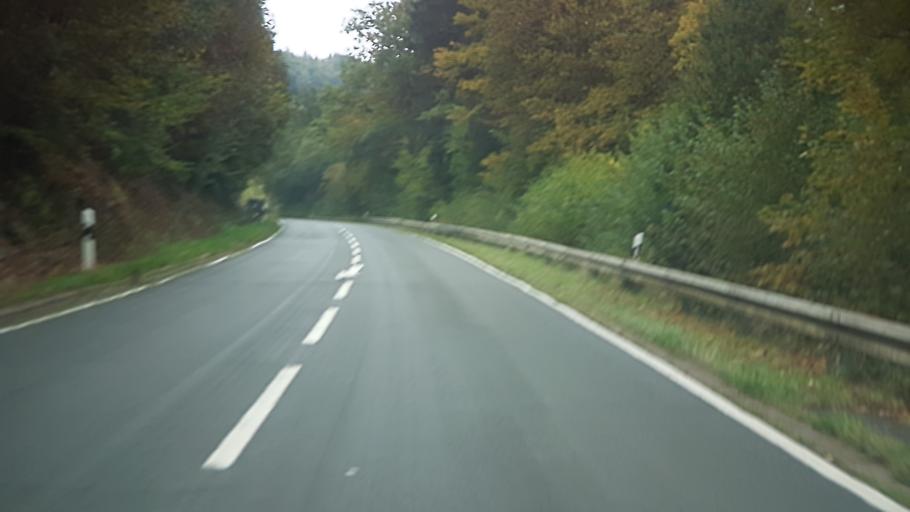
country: DE
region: North Rhine-Westphalia
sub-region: Regierungsbezirk Arnsberg
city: Herscheid
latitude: 51.2064
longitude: 7.6943
